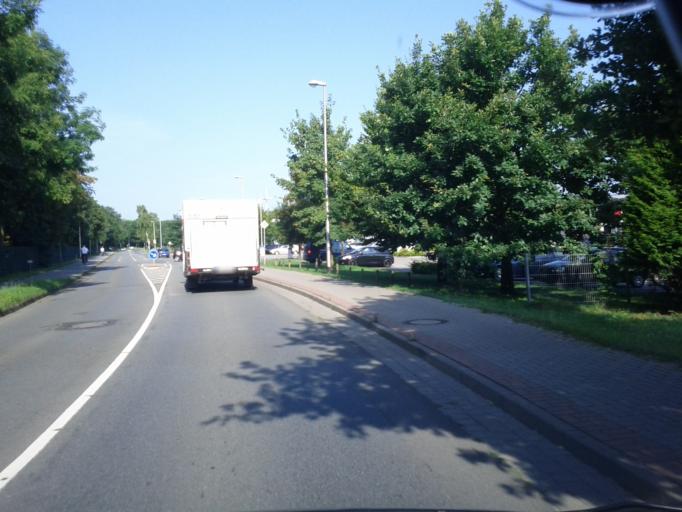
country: DE
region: Lower Saxony
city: Buxtehude
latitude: 53.4807
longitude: 9.6969
